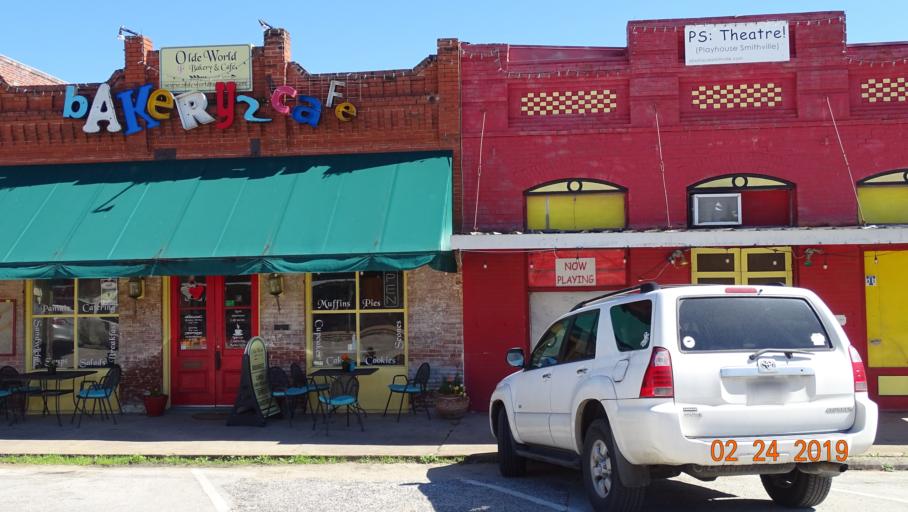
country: US
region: Texas
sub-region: Bastrop County
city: Smithville
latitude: 30.0073
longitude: -97.1602
